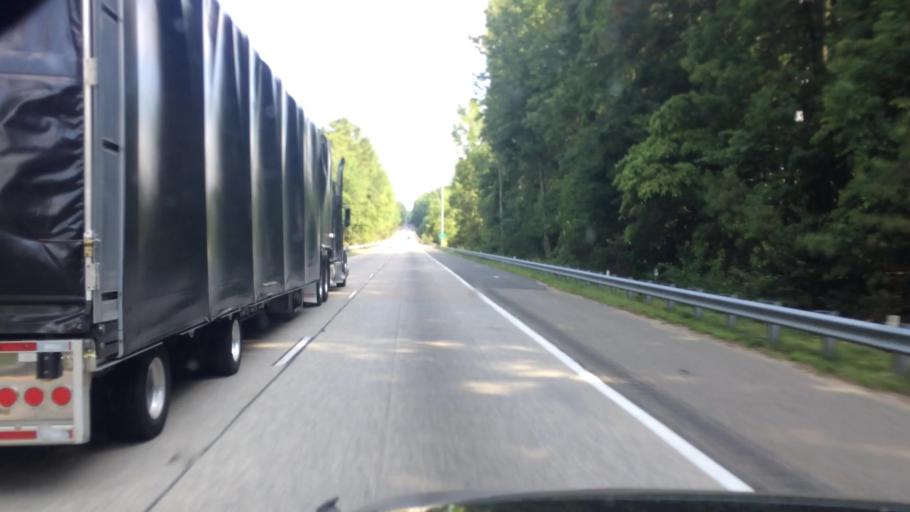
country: US
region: Virginia
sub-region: City of Williamsburg
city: Williamsburg
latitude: 37.2959
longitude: -76.6781
